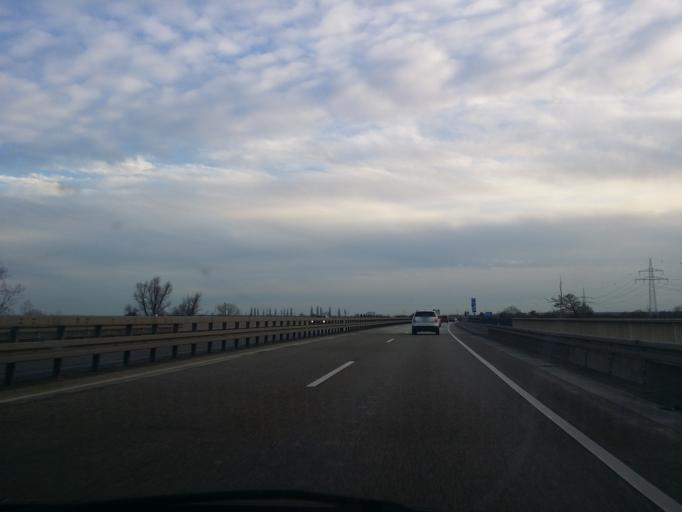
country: DE
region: Hesse
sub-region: Regierungsbezirk Darmstadt
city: Hochheim am Main
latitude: 50.0013
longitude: 8.3451
